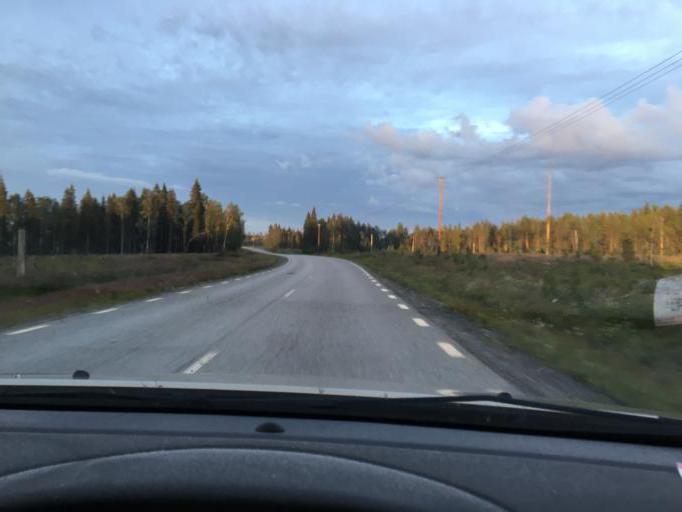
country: SE
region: Norrbotten
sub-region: Lulea Kommun
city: Ranea
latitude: 66.0411
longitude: 22.3024
